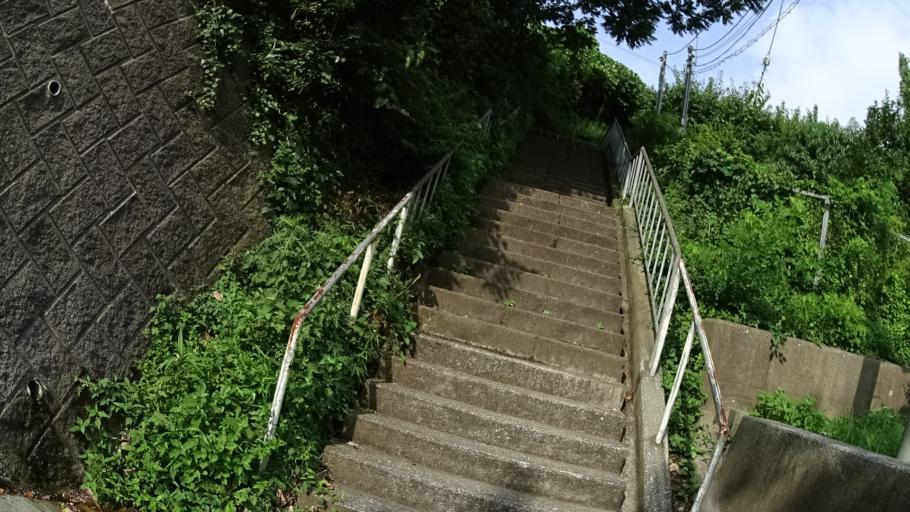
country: JP
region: Kanagawa
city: Zushi
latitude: 35.3187
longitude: 139.6060
